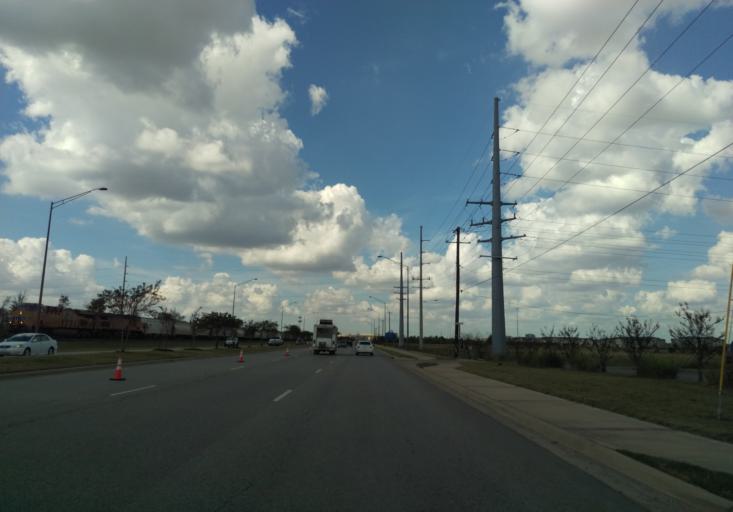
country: US
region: Texas
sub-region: Brazos County
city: College Station
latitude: 30.5807
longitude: -96.3215
